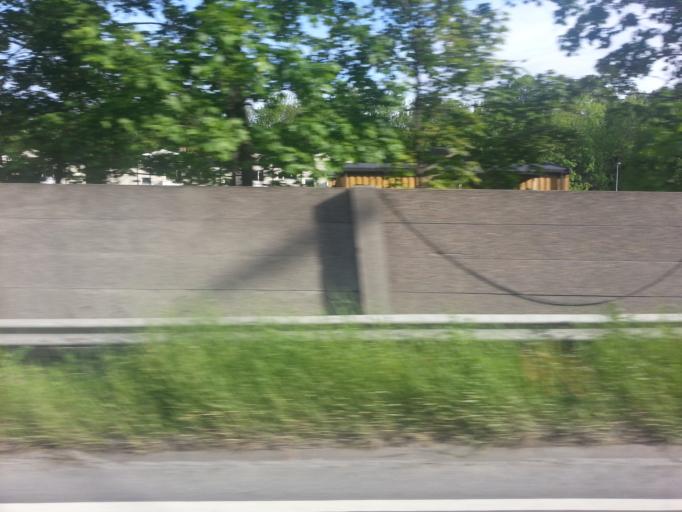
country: NO
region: Akershus
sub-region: Baerum
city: Lysaker
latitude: 59.9066
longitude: 10.6149
